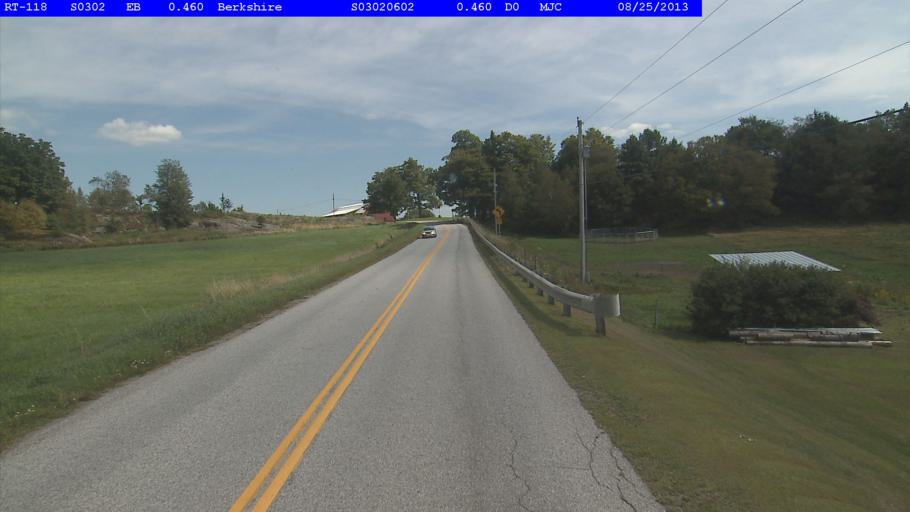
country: US
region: Vermont
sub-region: Franklin County
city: Enosburg Falls
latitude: 44.9848
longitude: -72.8063
